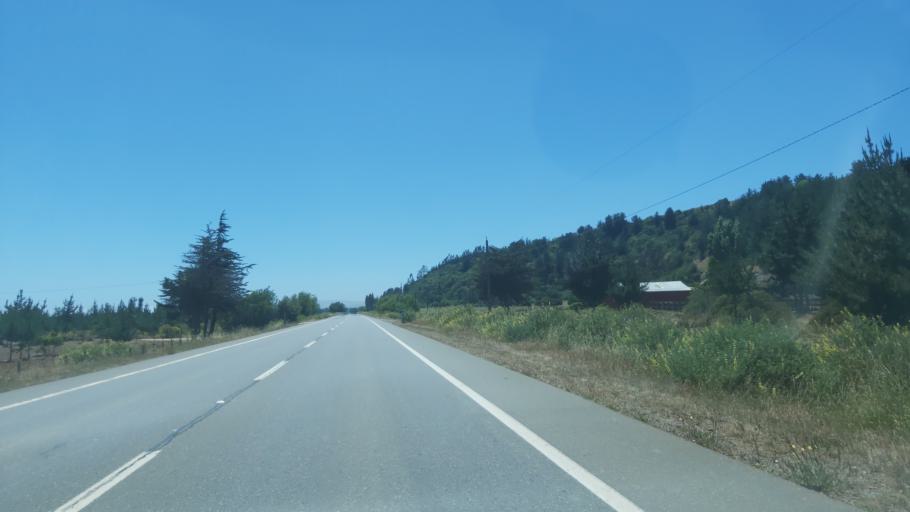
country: CL
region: Maule
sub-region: Provincia de Talca
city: Constitucion
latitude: -35.1674
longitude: -72.2629
